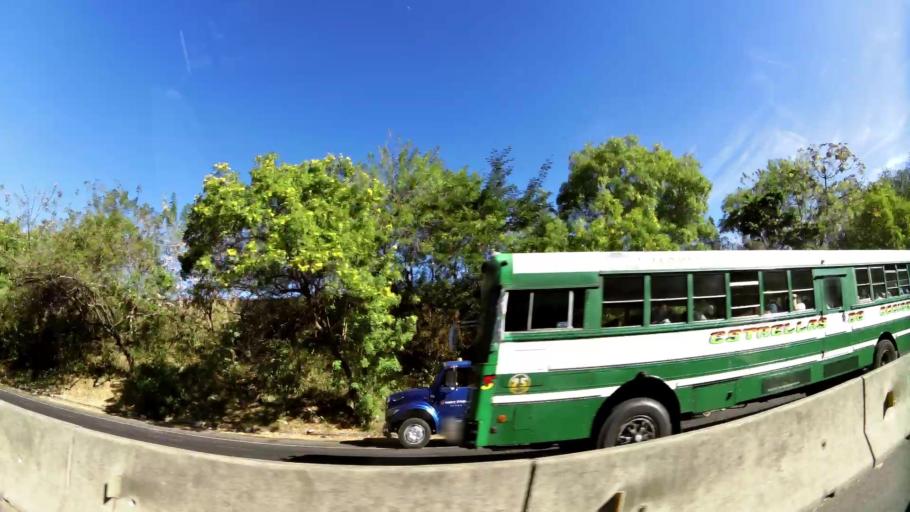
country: SV
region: Santa Ana
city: Santa Ana
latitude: 13.9554
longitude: -89.5714
